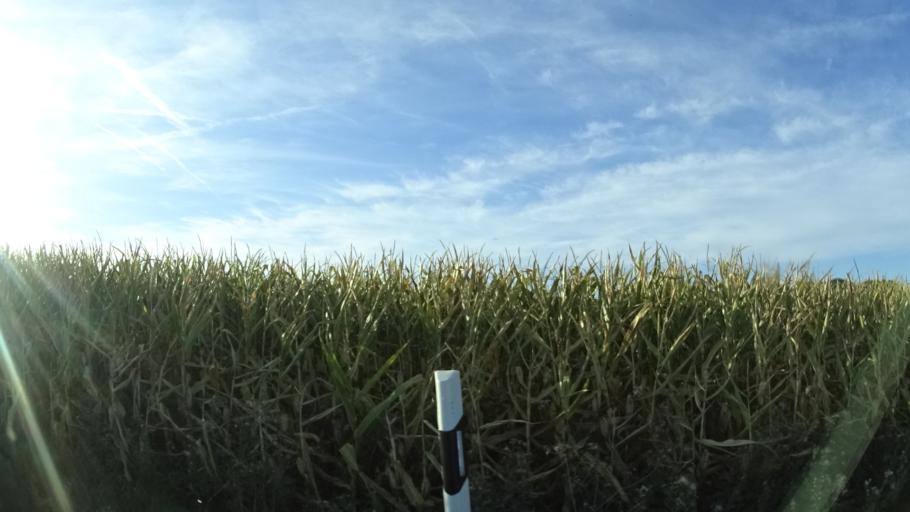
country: DE
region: Hesse
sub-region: Regierungsbezirk Darmstadt
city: Wachtersbach
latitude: 50.3009
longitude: 9.2682
